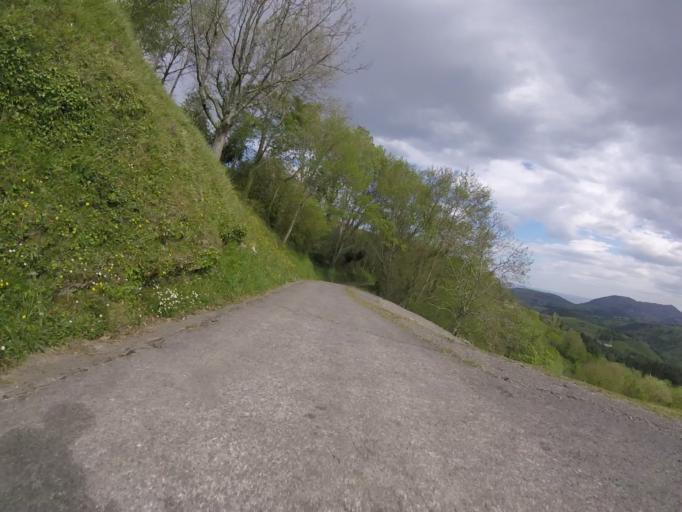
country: ES
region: Basque Country
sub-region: Provincia de Guipuzcoa
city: Zarautz
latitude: 43.2532
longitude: -2.1787
